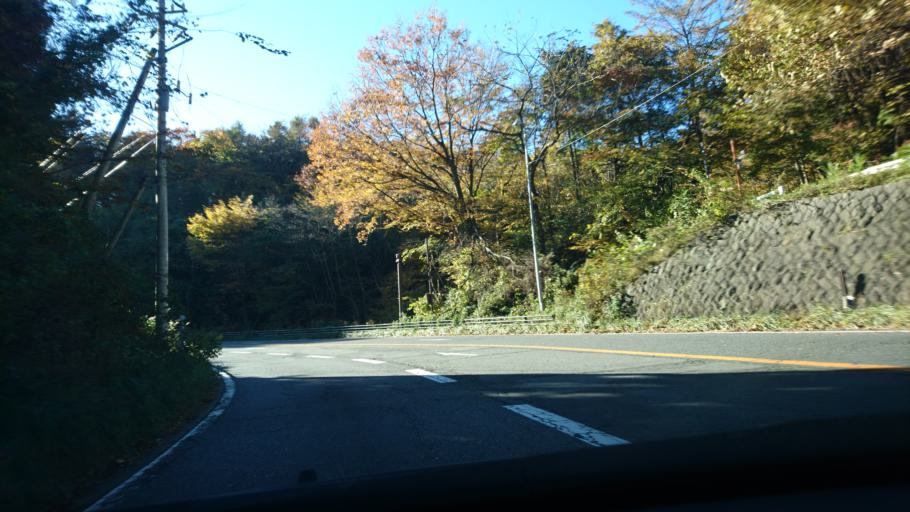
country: JP
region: Nagano
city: Saku
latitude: 36.3194
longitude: 138.6559
